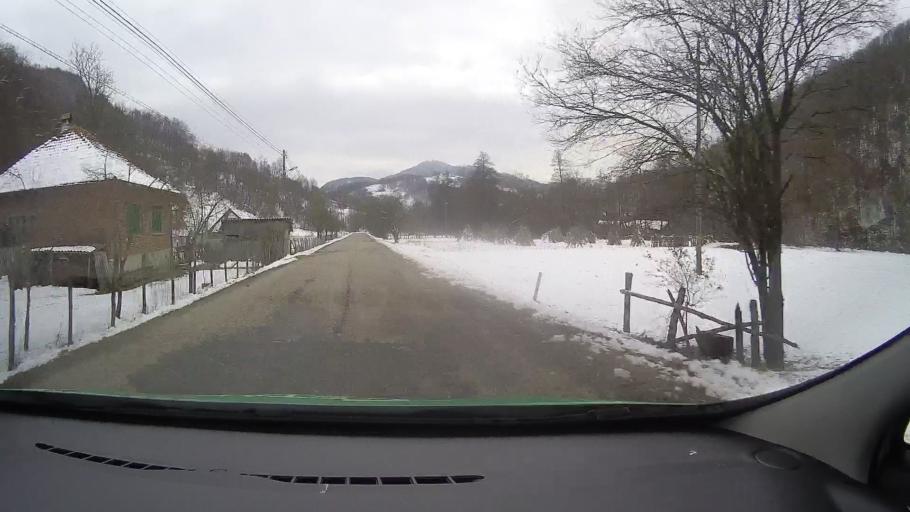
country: RO
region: Hunedoara
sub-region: Comuna Balsa
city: Balsa
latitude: 46.0509
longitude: 23.0709
